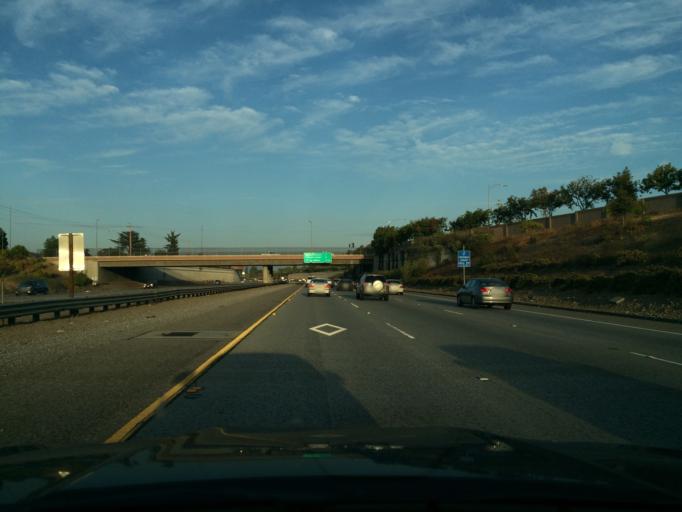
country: US
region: California
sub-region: Santa Clara County
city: Cambrian Park
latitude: 37.2512
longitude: -121.9333
